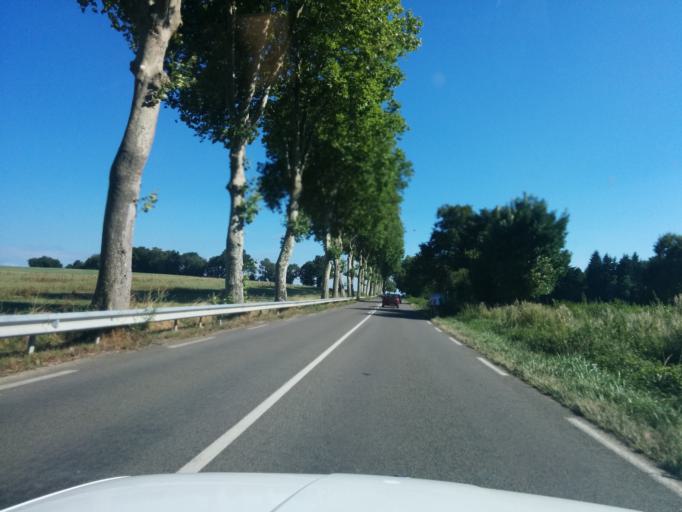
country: FR
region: Rhone-Alpes
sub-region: Departement de l'Ain
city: Meximieux
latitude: 45.9326
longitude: 5.1834
